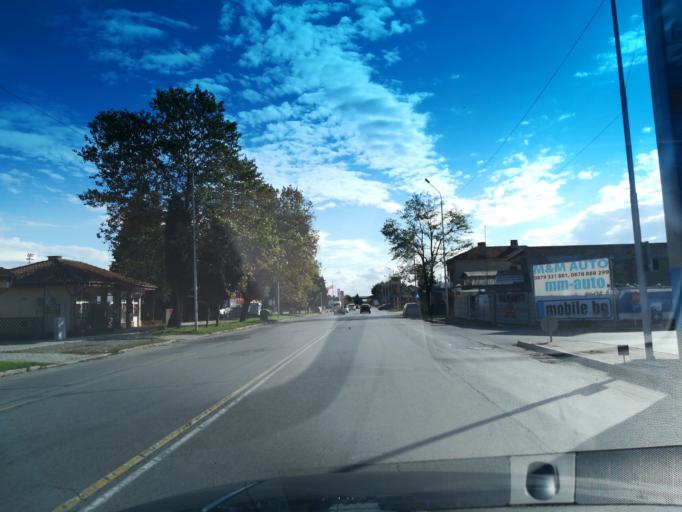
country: BG
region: Stara Zagora
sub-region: Obshtina Stara Zagora
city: Stara Zagora
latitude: 42.3970
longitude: 25.6449
